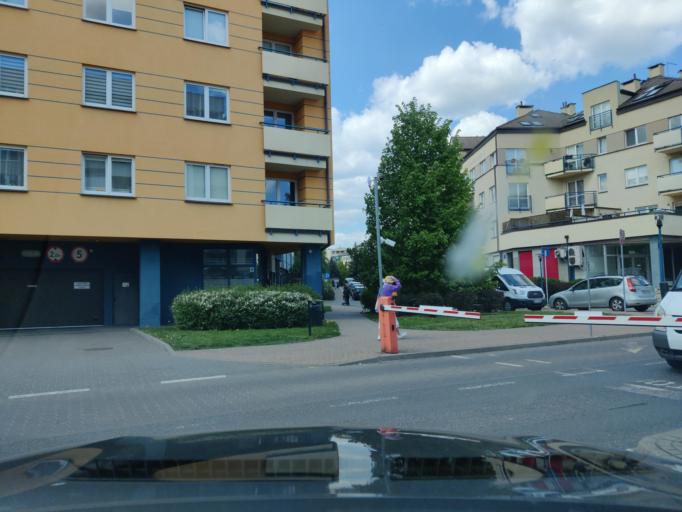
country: PL
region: Masovian Voivodeship
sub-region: Warszawa
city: Kabaty
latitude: 52.1324
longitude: 21.0710
